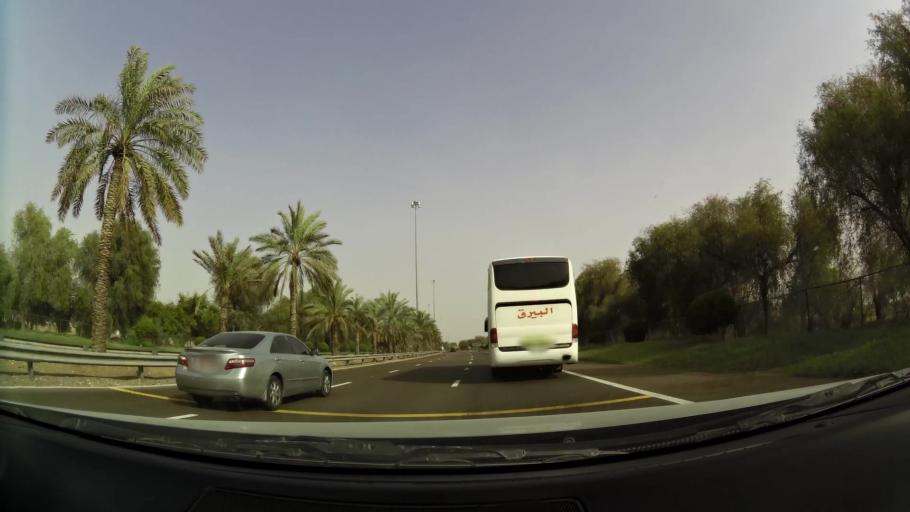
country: AE
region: Abu Dhabi
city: Al Ain
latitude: 24.1900
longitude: 55.5915
